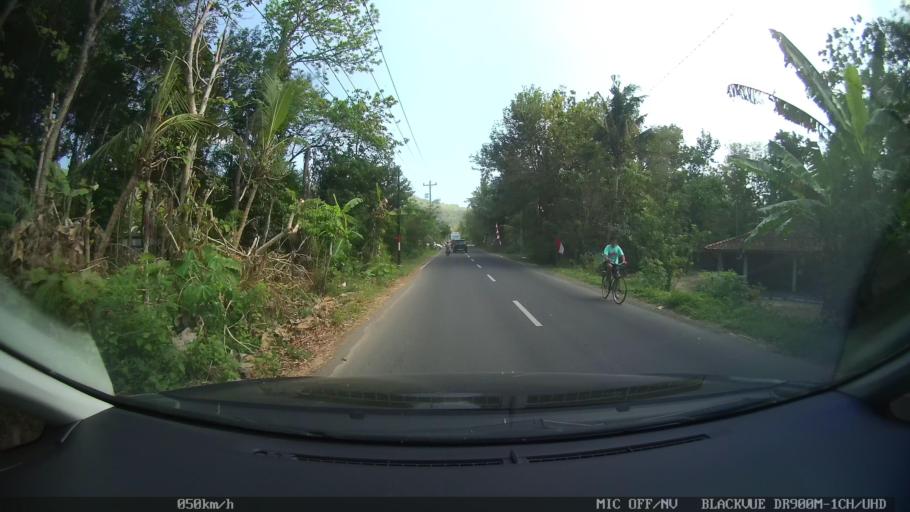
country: ID
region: Daerah Istimewa Yogyakarta
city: Pundong
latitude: -7.9798
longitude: 110.3383
